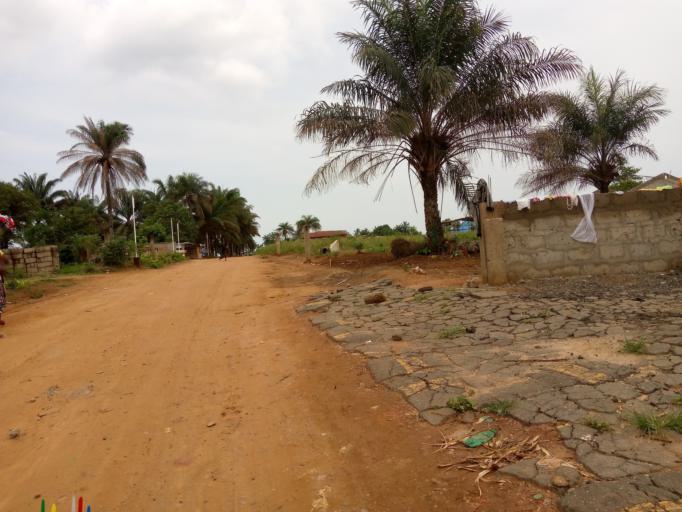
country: SL
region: Western Area
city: Waterloo
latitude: 8.3369
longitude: -13.0178
